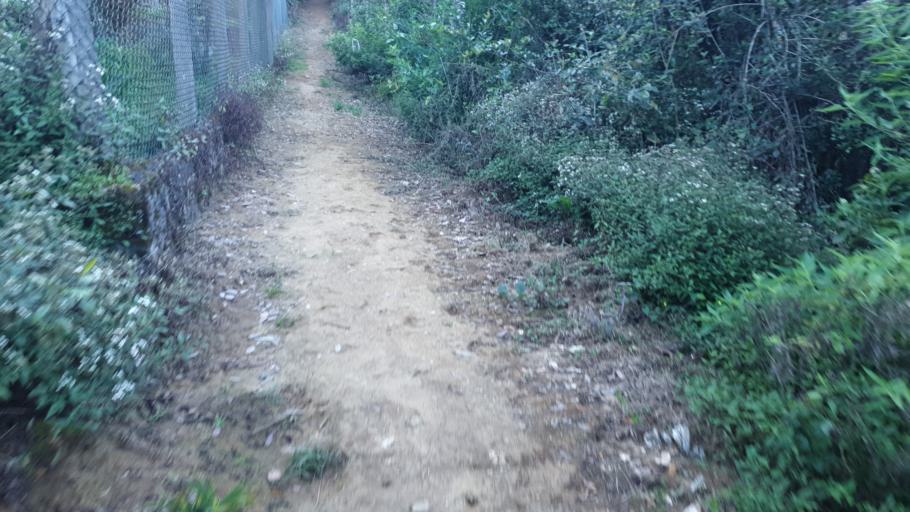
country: LK
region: Central
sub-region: Nuwara Eliya District
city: Nuwara Eliya
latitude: 6.9591
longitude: 80.7621
